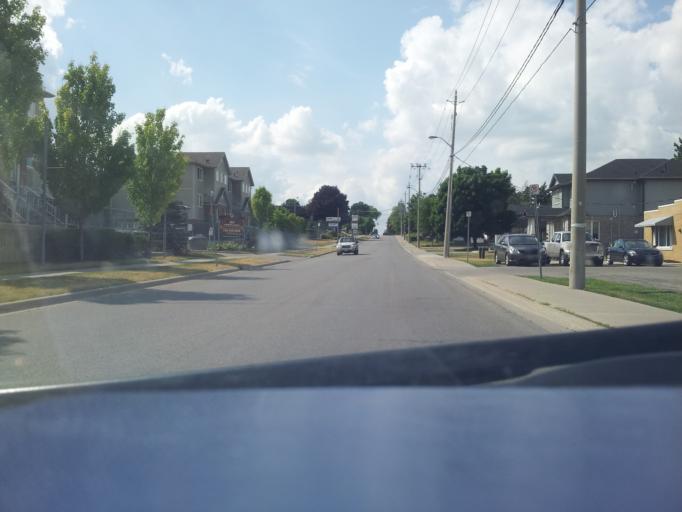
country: CA
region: Ontario
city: Kitchener
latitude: 43.4399
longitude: -80.5121
